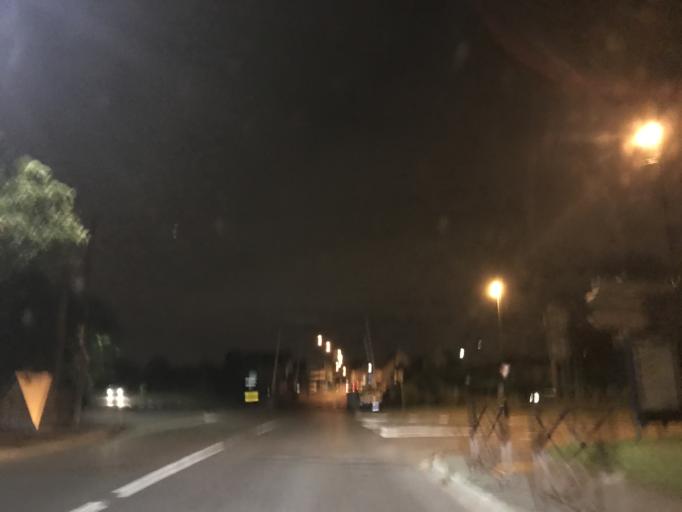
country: FR
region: Ile-de-France
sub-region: Departement des Yvelines
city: Sartrouville
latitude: 48.9419
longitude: 2.2000
